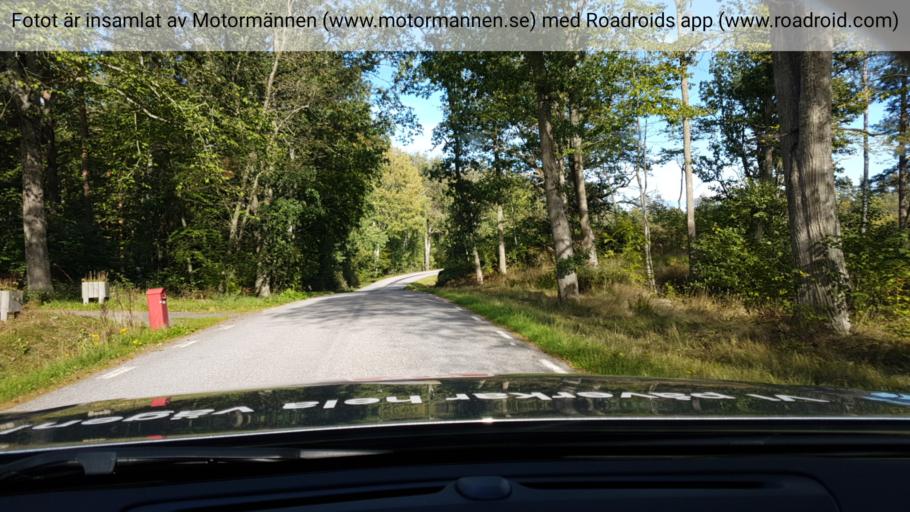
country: SE
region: OEstergoetland
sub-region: Valdemarsviks Kommun
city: Valdemarsvik
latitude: 58.1085
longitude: 16.6433
